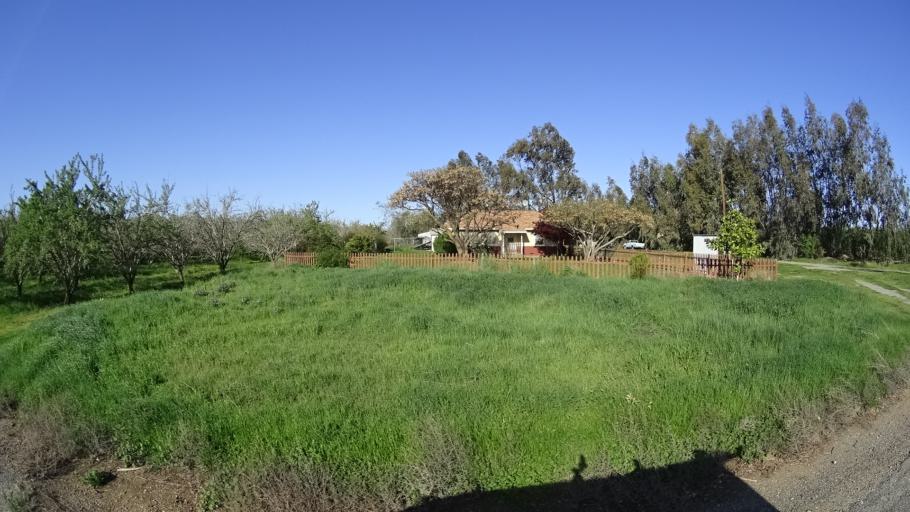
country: US
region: California
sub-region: Glenn County
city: Orland
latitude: 39.7624
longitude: -122.1228
